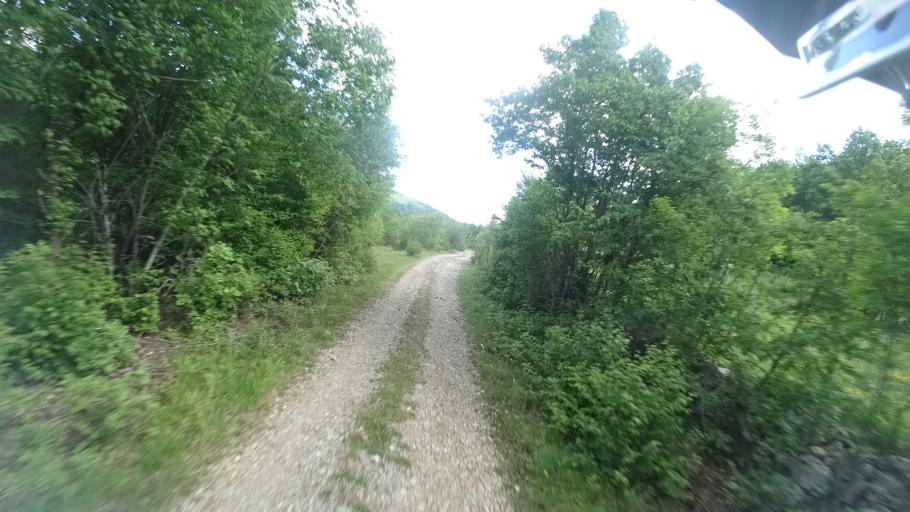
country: HR
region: Zadarska
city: Gracac
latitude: 44.2702
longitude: 15.9270
